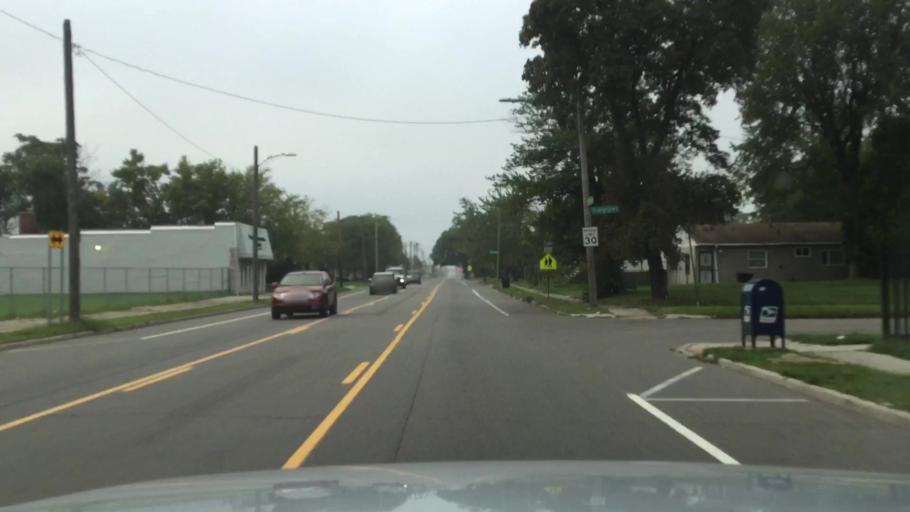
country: US
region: Michigan
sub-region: Wayne County
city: Dearborn
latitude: 42.3693
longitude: -83.1584
